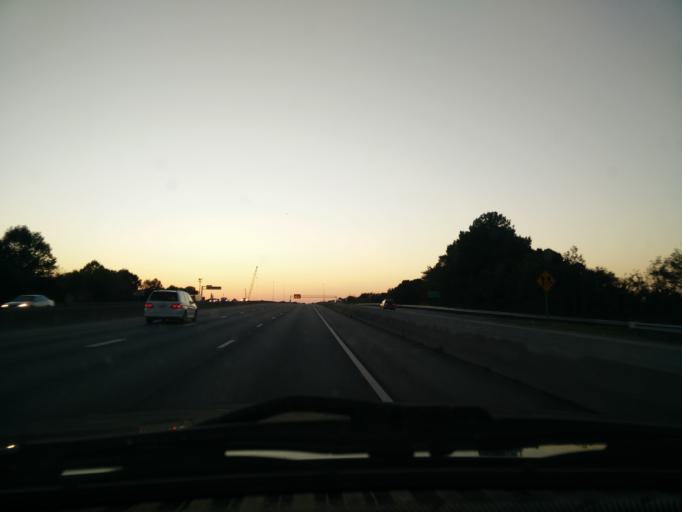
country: US
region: Virginia
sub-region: City of Chesapeake
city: Chesapeake
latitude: 36.8461
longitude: -76.1799
